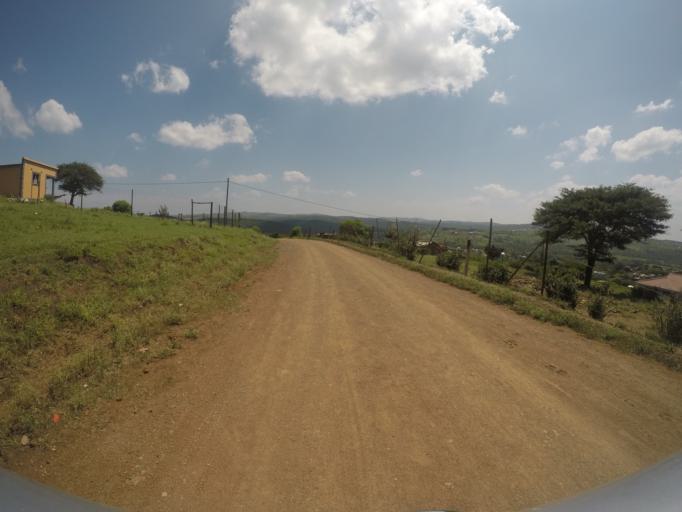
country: ZA
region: KwaZulu-Natal
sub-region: uThungulu District Municipality
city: Empangeni
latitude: -28.5975
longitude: 31.7394
